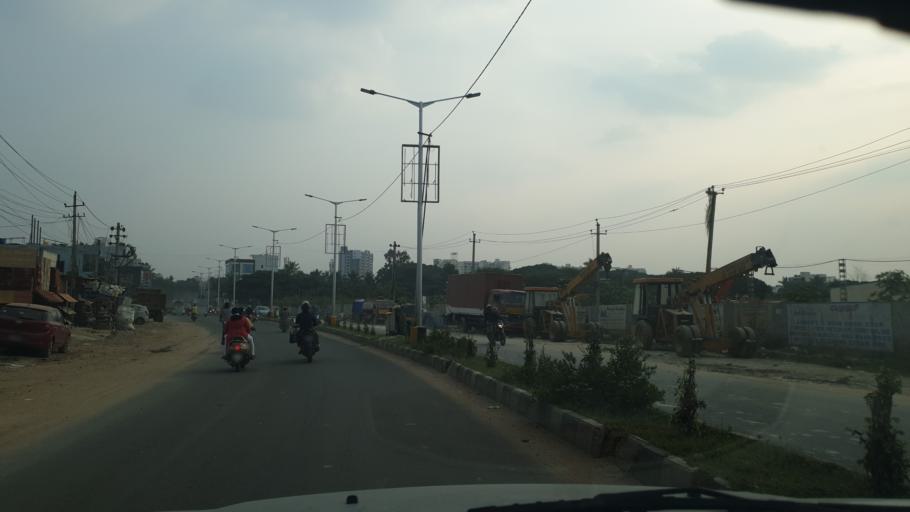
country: IN
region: Karnataka
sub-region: Bangalore Urban
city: Yelahanka
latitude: 13.0412
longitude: 77.6416
